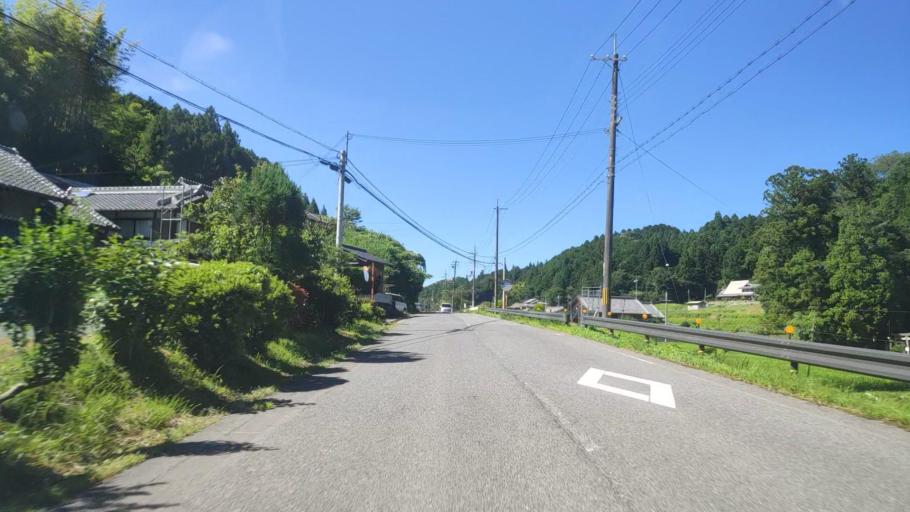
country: JP
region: Nara
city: Haibara-akanedai
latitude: 34.4440
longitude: 135.9380
